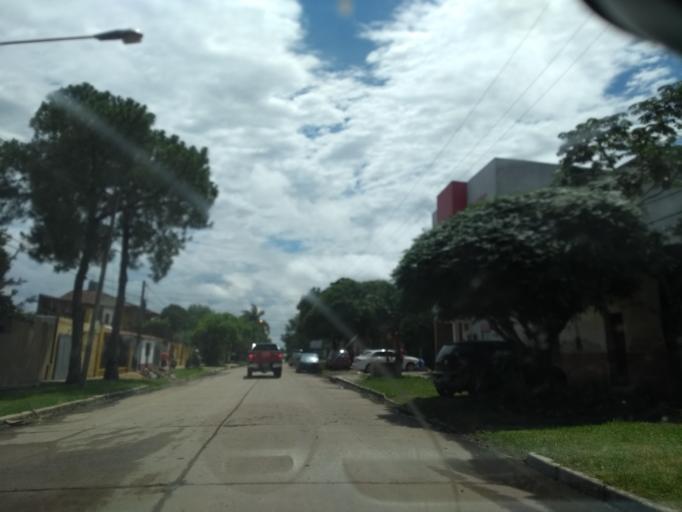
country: AR
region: Chaco
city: Barranqueras
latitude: -27.4819
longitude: -58.9495
